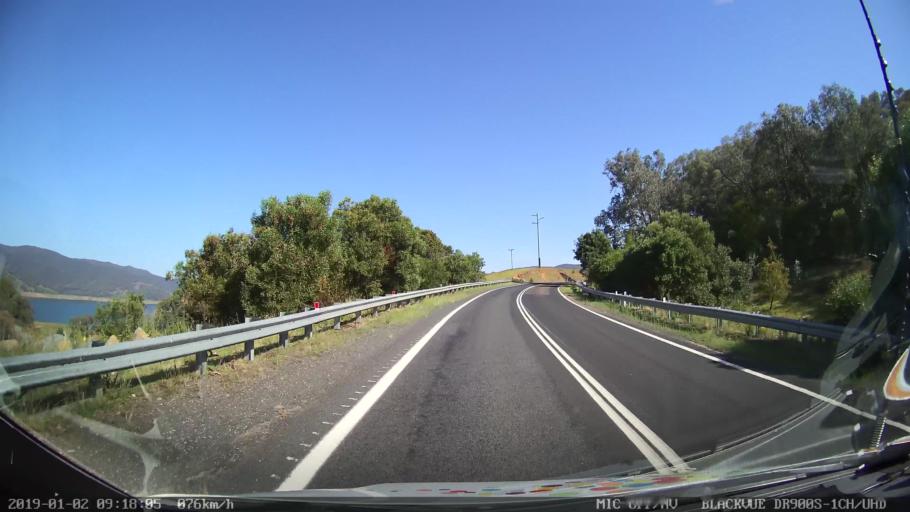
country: AU
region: New South Wales
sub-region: Tumut Shire
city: Tumut
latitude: -35.4328
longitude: 148.2858
